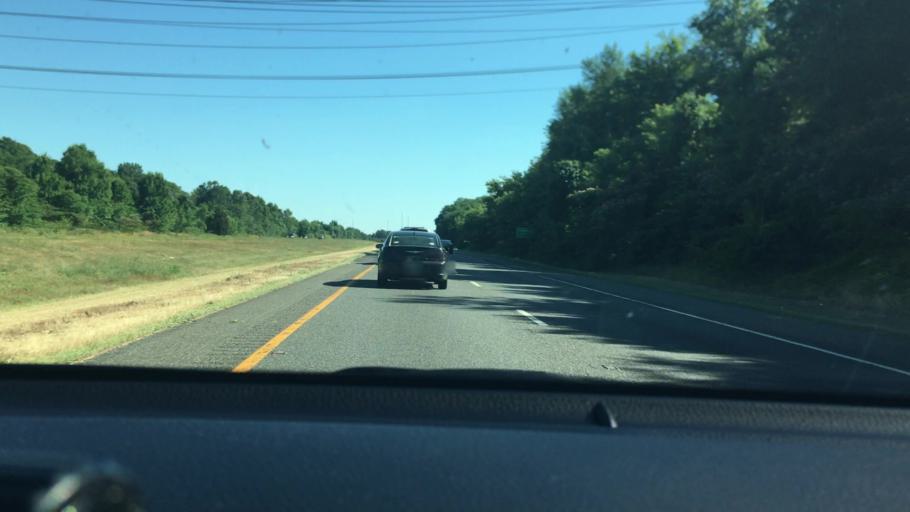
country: US
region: New Jersey
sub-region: Gloucester County
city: Richwood
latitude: 39.7299
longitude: -75.1513
